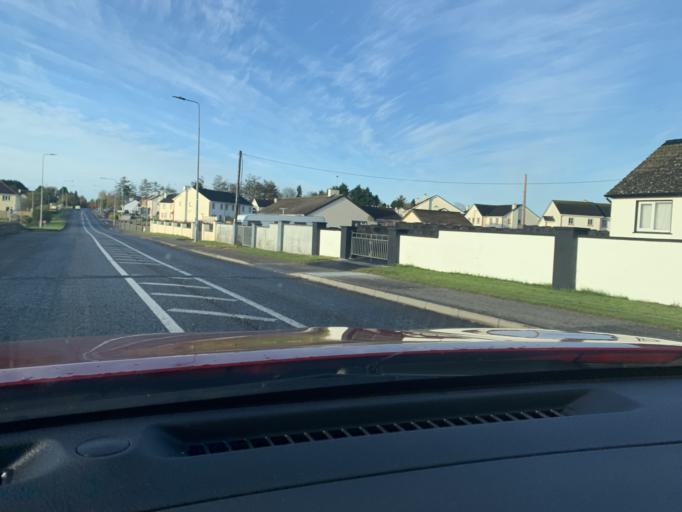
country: IE
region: Connaught
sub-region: Roscommon
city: Ballaghaderreen
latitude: 53.9073
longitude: -8.5636
